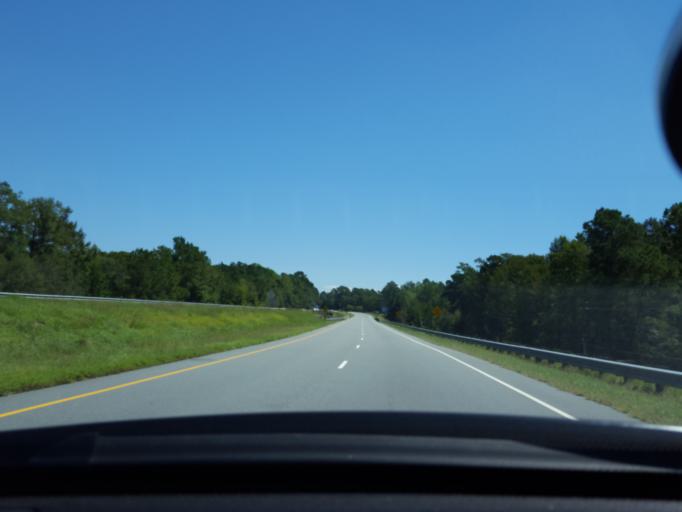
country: US
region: North Carolina
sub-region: Bladen County
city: Elizabethtown
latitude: 34.6470
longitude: -78.5591
